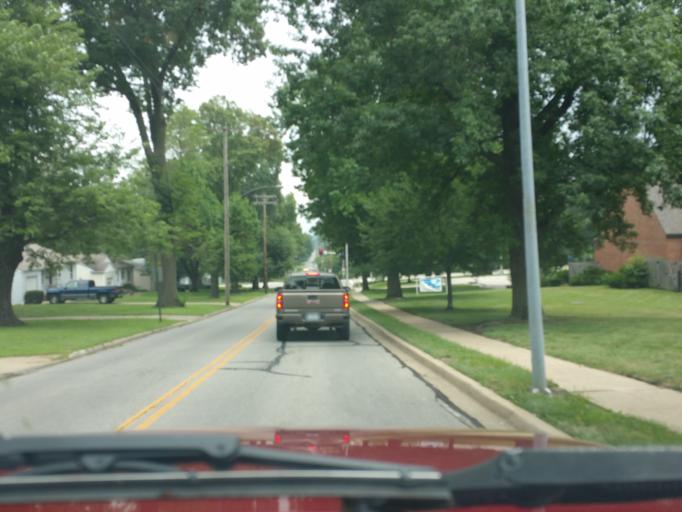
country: US
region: Kansas
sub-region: Johnson County
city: Fairway
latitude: 39.0151
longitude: -94.6416
